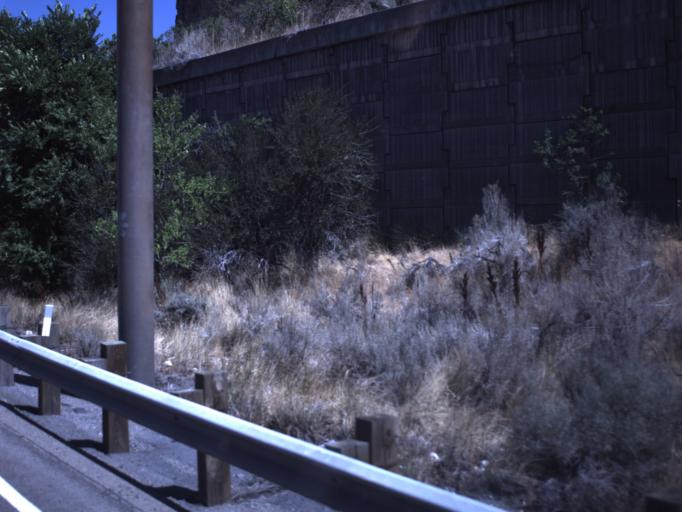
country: US
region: Utah
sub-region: Utah County
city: Orem
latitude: 40.3144
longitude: -111.6547
